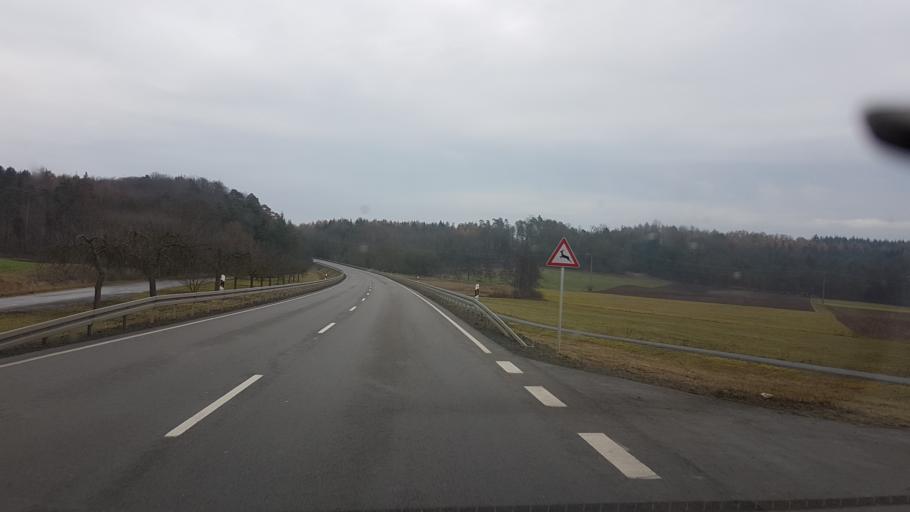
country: DE
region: Bavaria
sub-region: Regierungsbezirk Unterfranken
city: Bundorf
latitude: 50.2574
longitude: 10.5466
